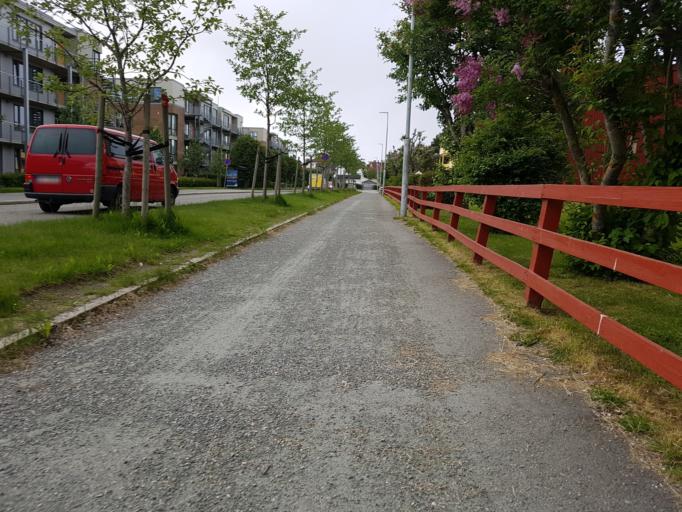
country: NO
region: Sor-Trondelag
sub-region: Trondheim
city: Trondheim
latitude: 63.4321
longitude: 10.4487
